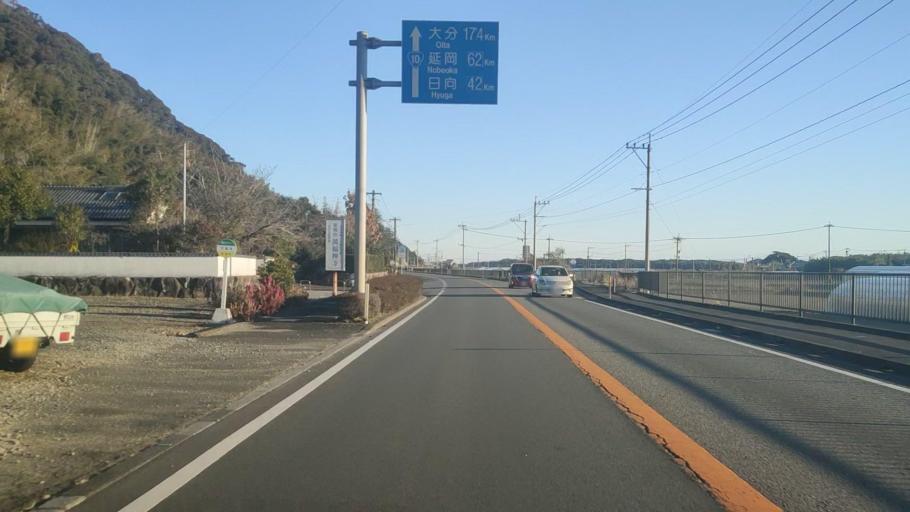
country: JP
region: Miyazaki
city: Takanabe
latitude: 32.0905
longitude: 131.5142
